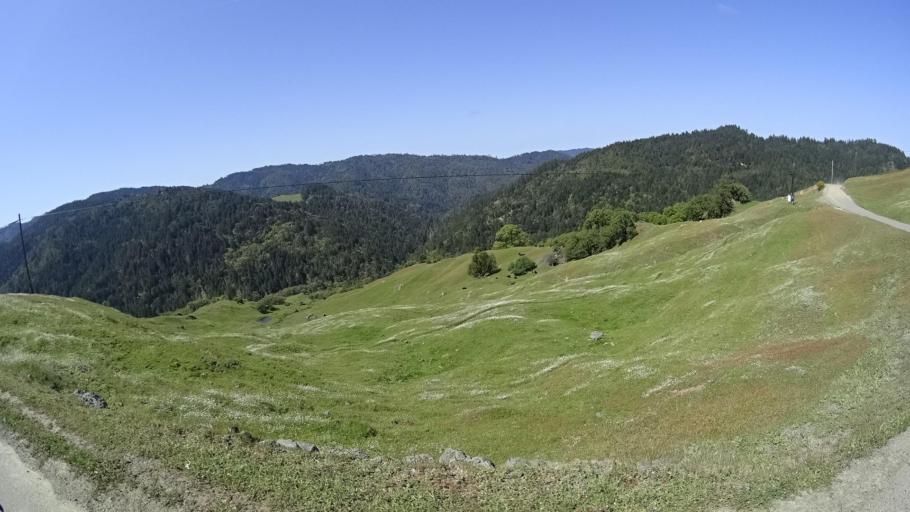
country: US
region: California
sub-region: Humboldt County
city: Redway
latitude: 40.0248
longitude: -123.6309
